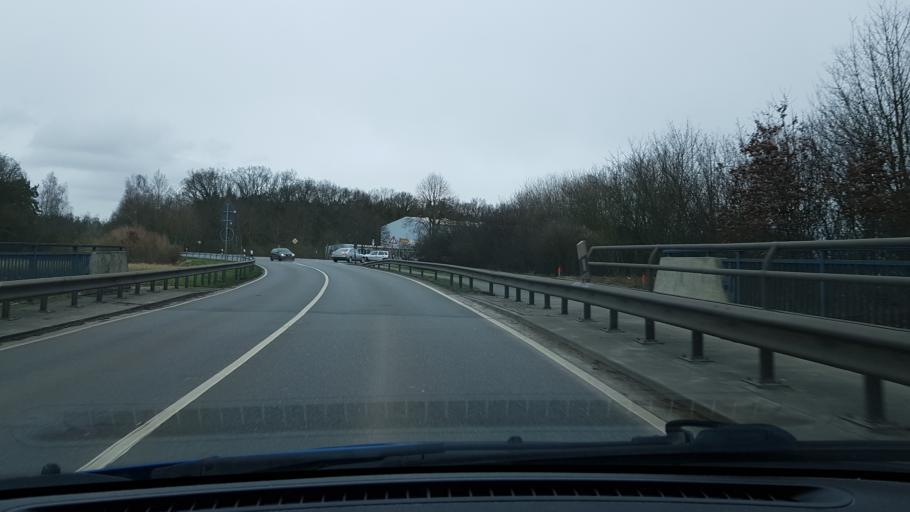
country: DE
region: Lower Saxony
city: Uelzen
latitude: 52.9858
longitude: 10.5686
